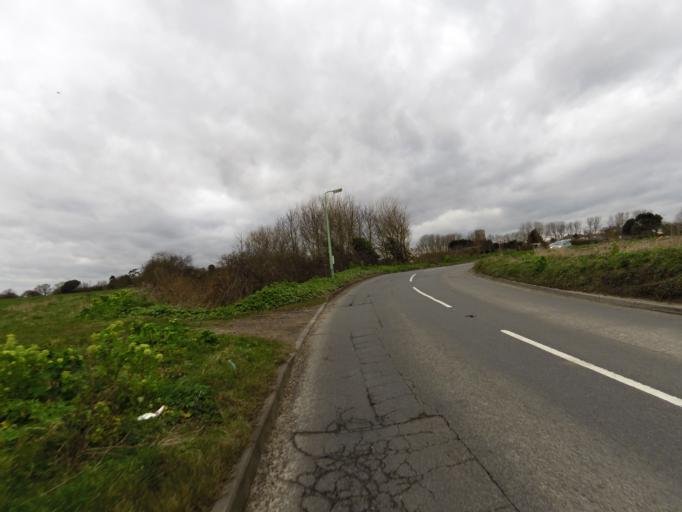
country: GB
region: England
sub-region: Norfolk
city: Hopton on Sea
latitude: 52.5189
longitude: 1.7432
